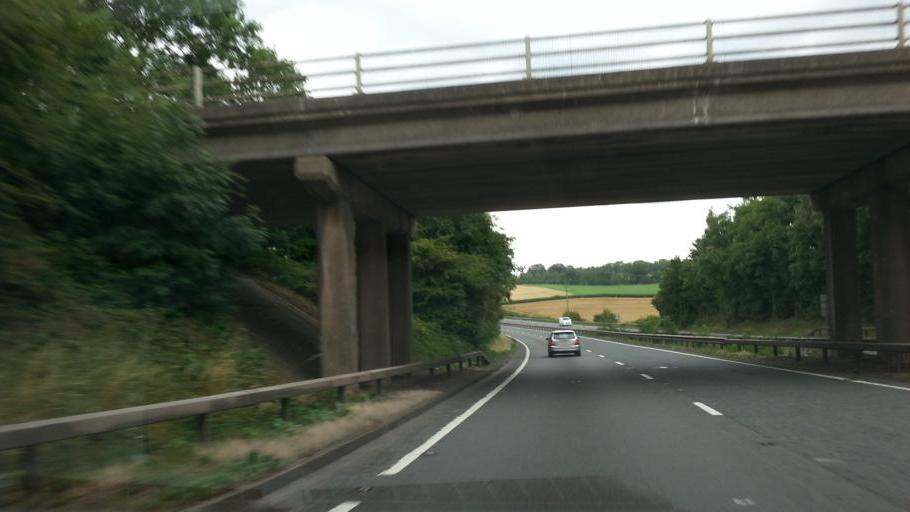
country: GB
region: England
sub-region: Herefordshire
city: Marstow
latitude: 51.8679
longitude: -2.6316
